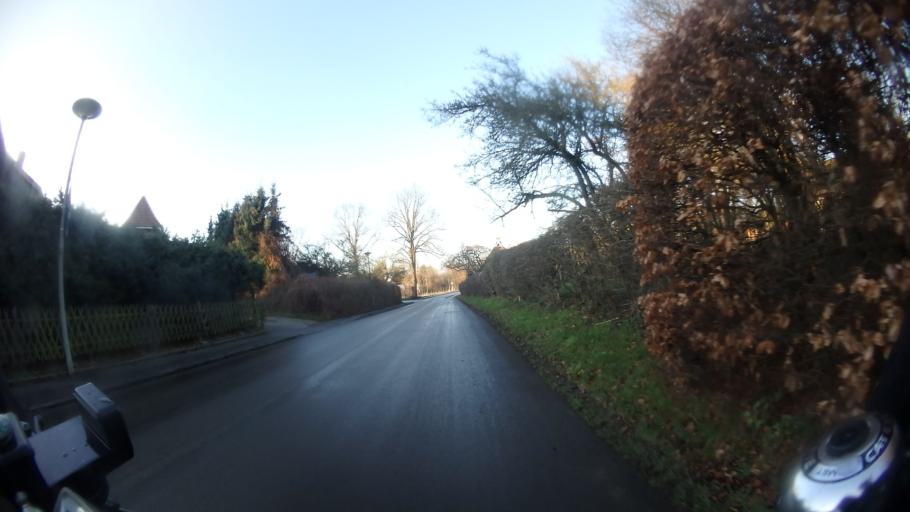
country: DE
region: Schleswig-Holstein
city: Travemuende
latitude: 53.9859
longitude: 10.8623
